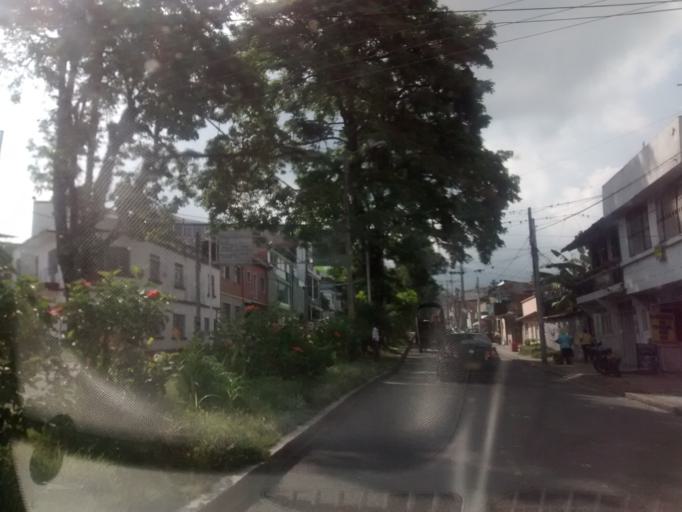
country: CO
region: Tolima
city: Ibague
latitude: 4.4458
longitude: -75.2327
